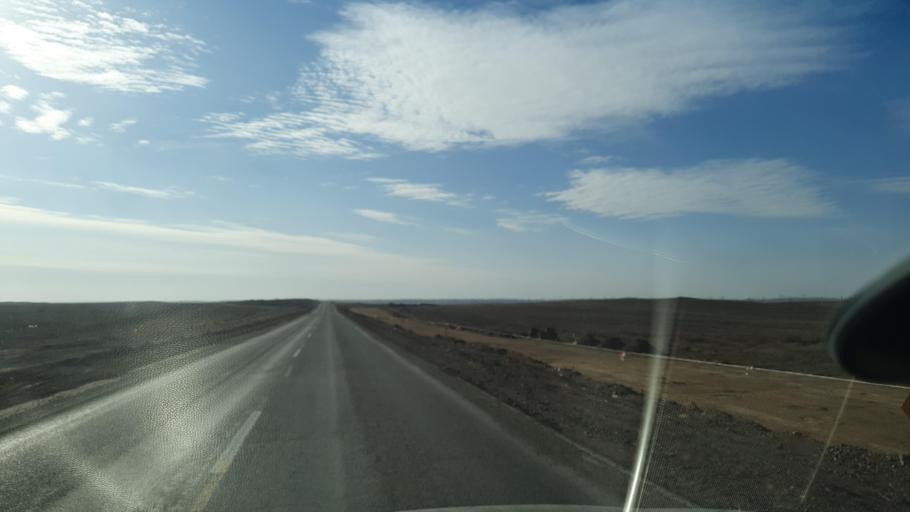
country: KZ
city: Priozersk
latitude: 45.8772
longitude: 73.4835
